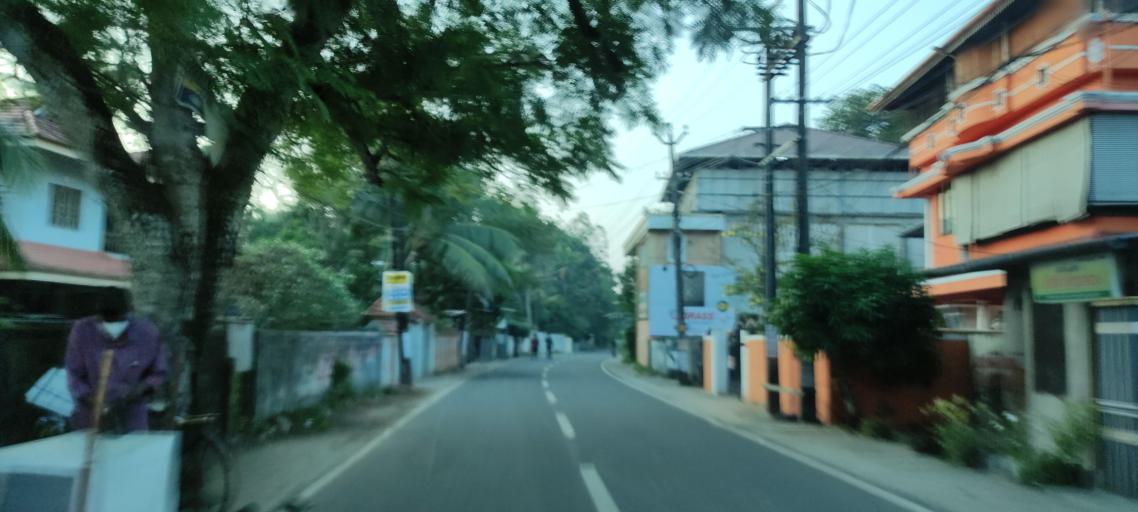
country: IN
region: Kerala
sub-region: Alappuzha
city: Alleppey
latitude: 9.4602
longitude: 76.3442
